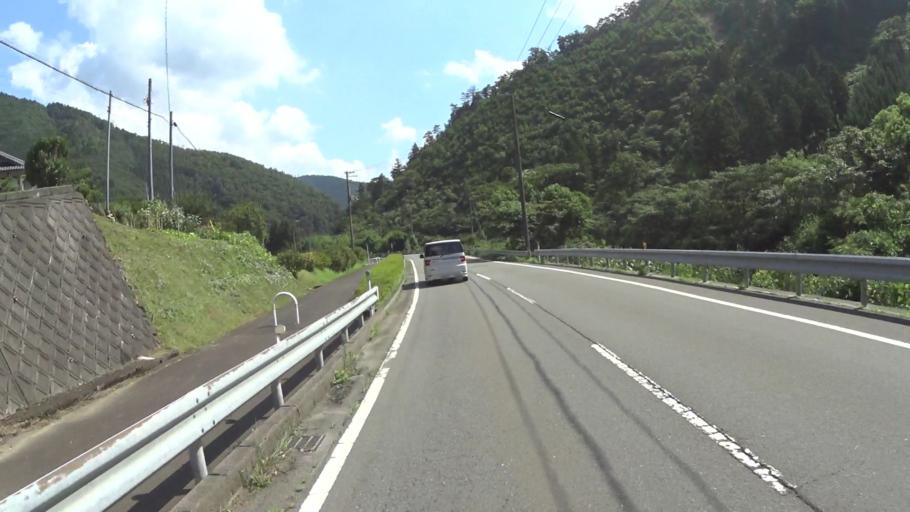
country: JP
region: Kyoto
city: Maizuru
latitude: 35.3062
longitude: 135.5556
